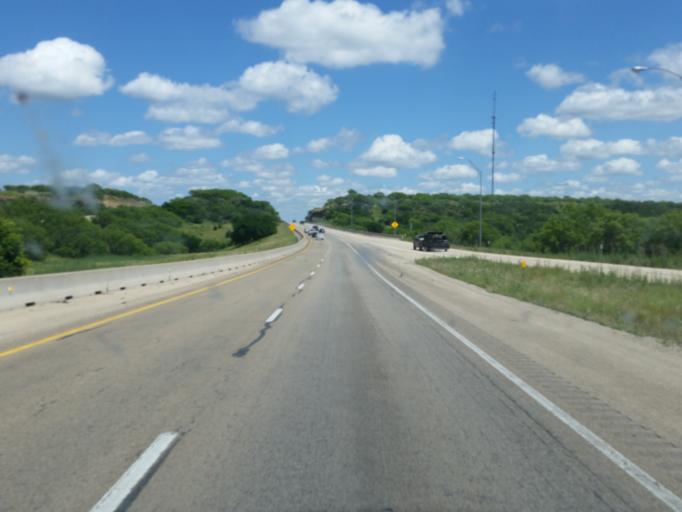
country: US
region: Texas
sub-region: Callahan County
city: Baird
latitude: 32.3965
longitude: -99.3682
